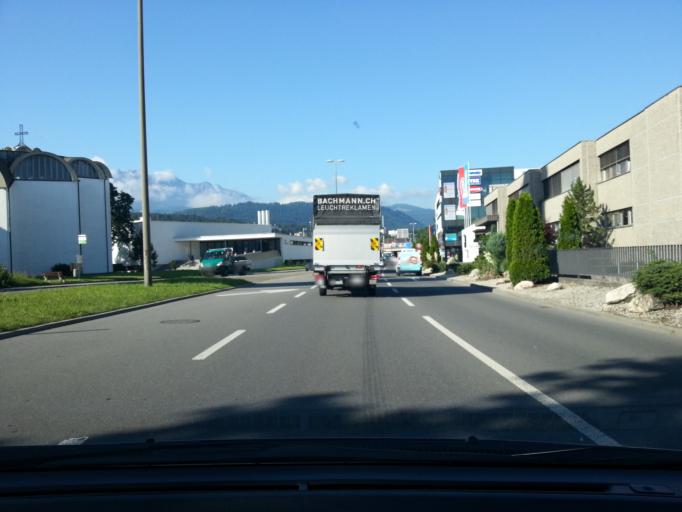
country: CH
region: Lucerne
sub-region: Hochdorf District
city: Emmen
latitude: 47.0715
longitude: 8.2855
